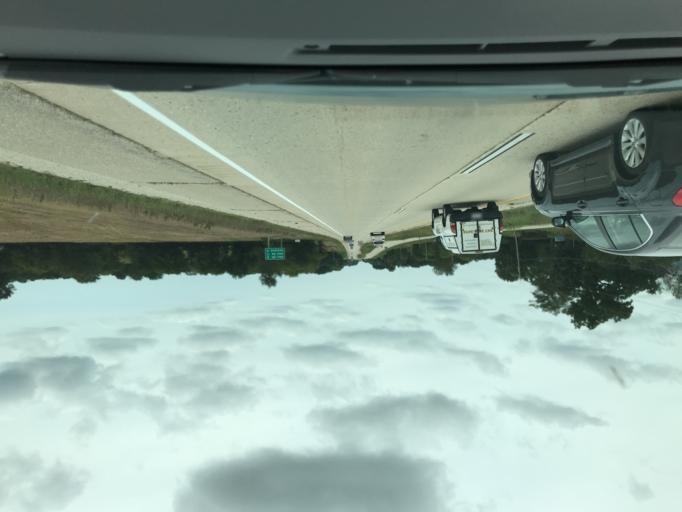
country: US
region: Wisconsin
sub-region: Kenosha County
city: Paddock Lake
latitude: 42.5680
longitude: -88.0881
